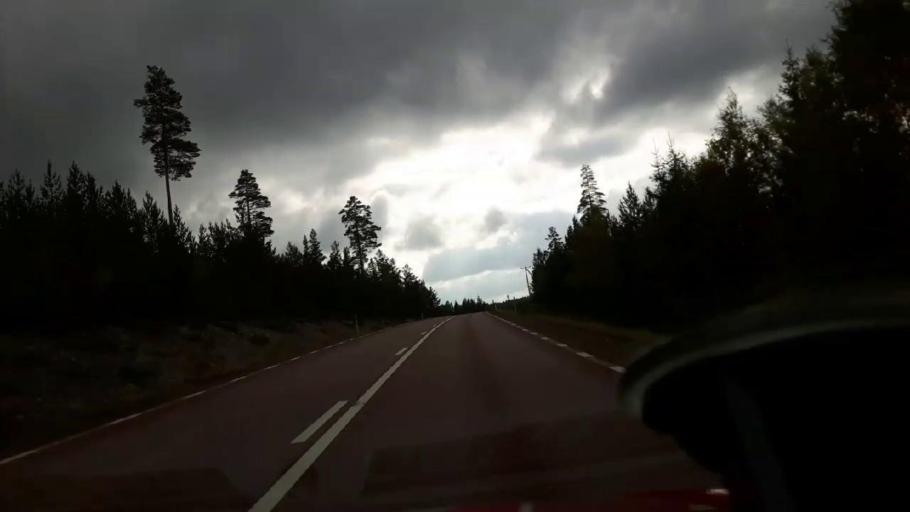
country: SE
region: Gaevleborg
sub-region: Soderhamns Kommun
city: Ljusne
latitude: 61.1201
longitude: 16.9351
